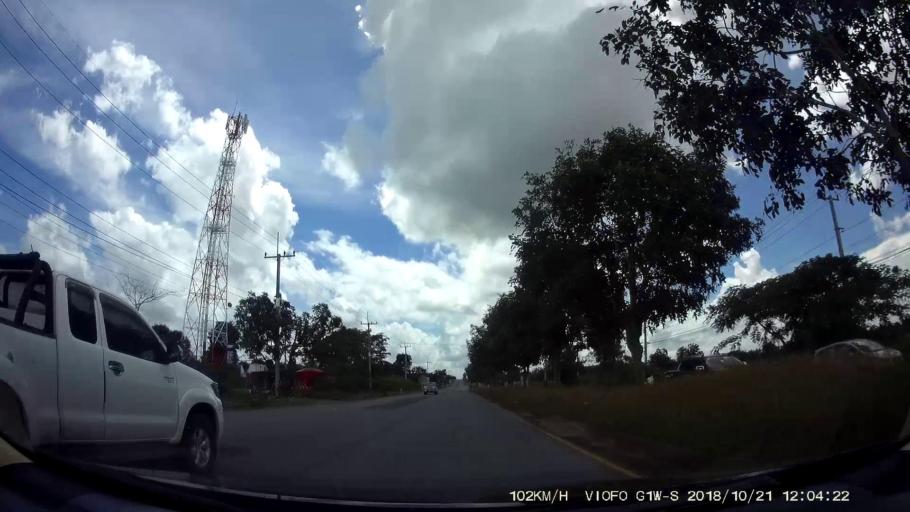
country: TH
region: Chaiyaphum
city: Chatturat
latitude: 15.4955
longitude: 101.8211
